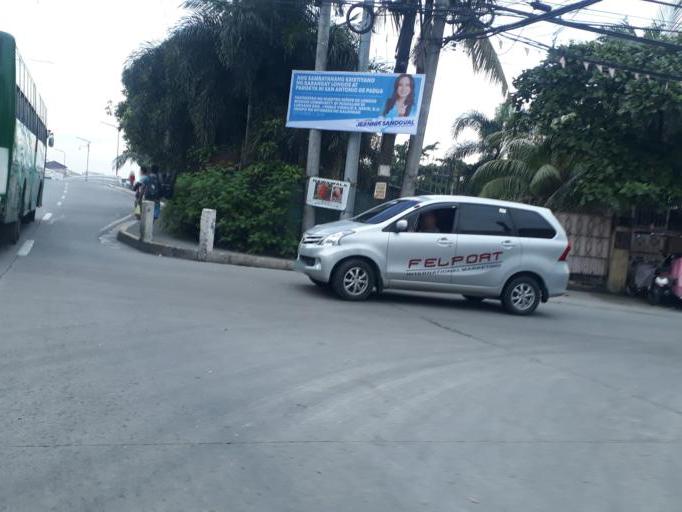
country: PH
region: Metro Manila
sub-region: Caloocan City
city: Niugan
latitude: 14.6556
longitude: 120.9572
